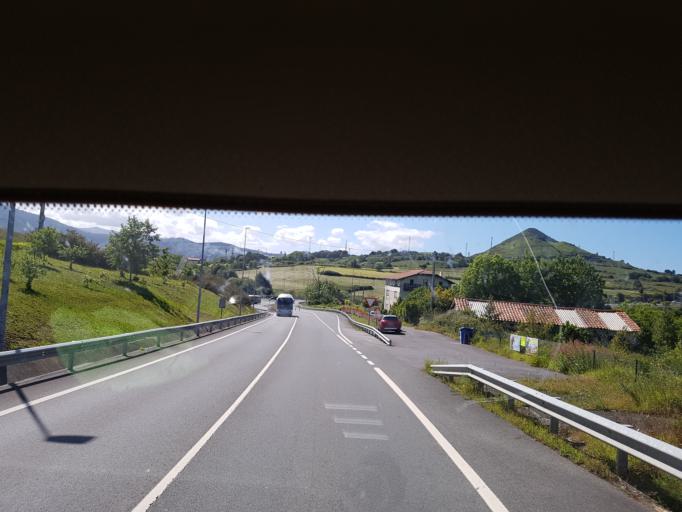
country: ES
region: Basque Country
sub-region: Bizkaia
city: Urtuella
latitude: 43.3226
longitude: -3.0766
